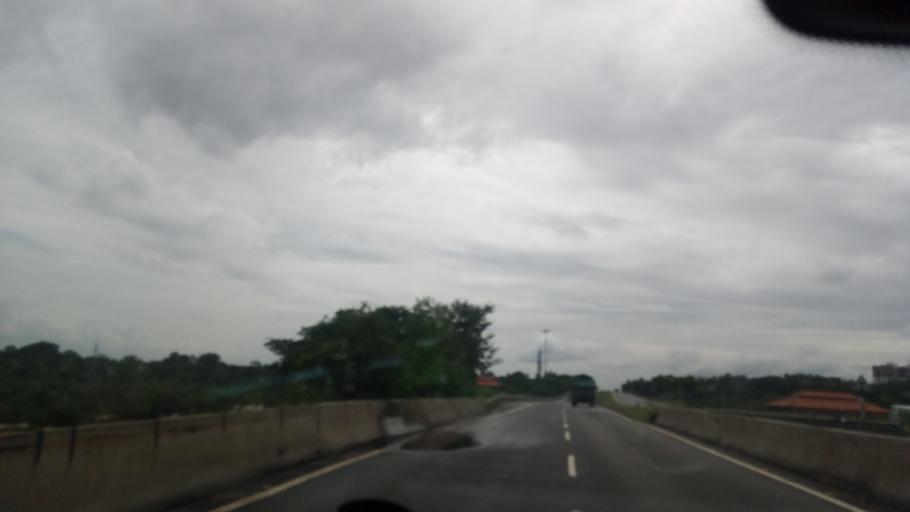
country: IN
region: Karnataka
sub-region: Bangalore Urban
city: Bangalore
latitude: 12.8574
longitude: 77.5277
